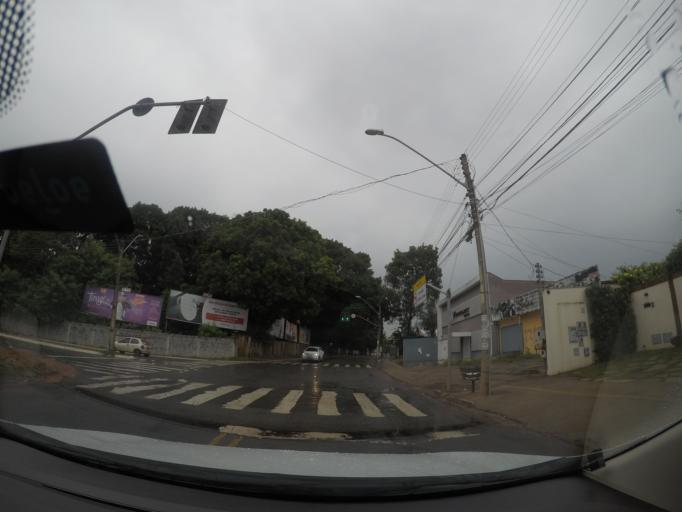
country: BR
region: Goias
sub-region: Goiania
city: Goiania
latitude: -16.6886
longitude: -49.2453
